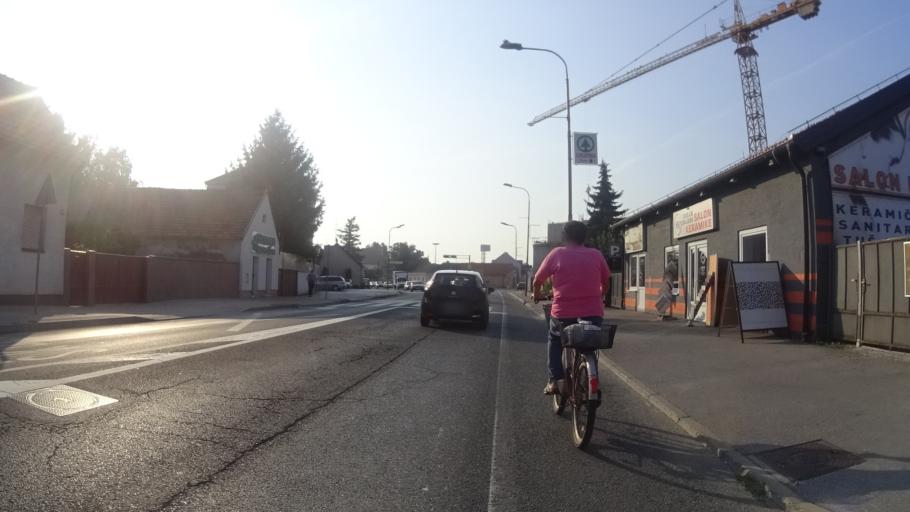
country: HR
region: Varazdinska
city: Varazdin
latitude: 46.3141
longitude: 16.3282
